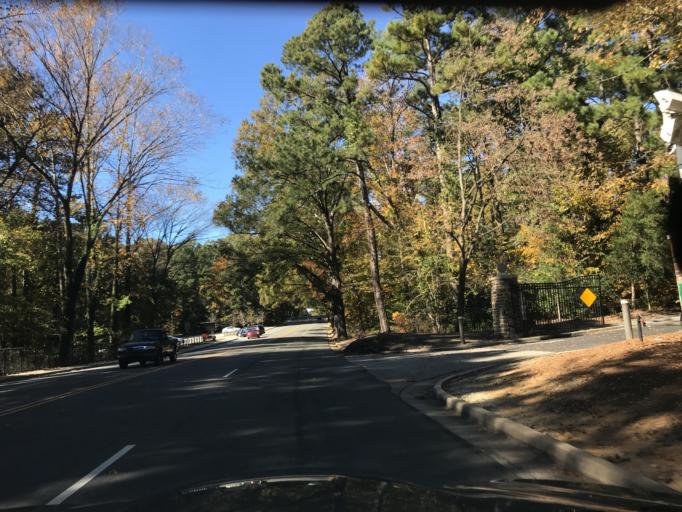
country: US
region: North Carolina
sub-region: Durham County
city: Durham
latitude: 35.9929
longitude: -78.9438
